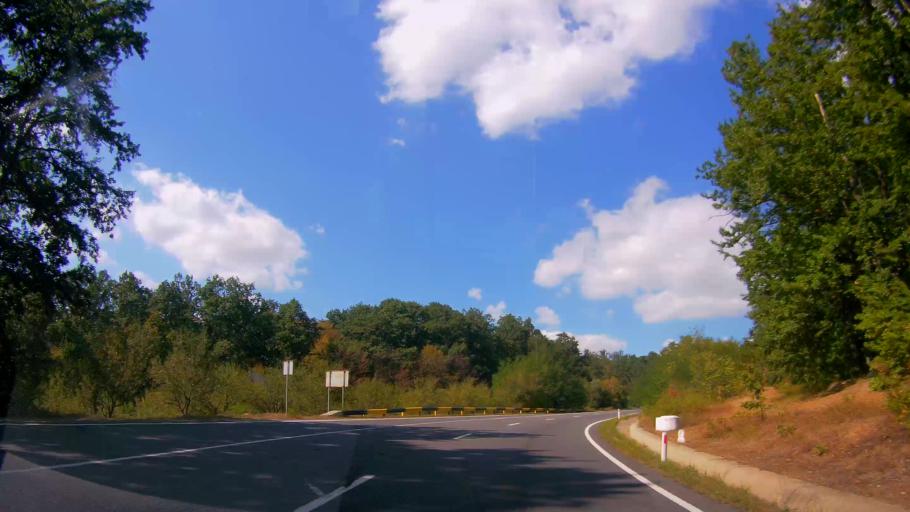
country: RO
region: Salaj
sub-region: Comuna Treznea
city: Treznea
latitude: 47.1370
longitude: 23.1197
